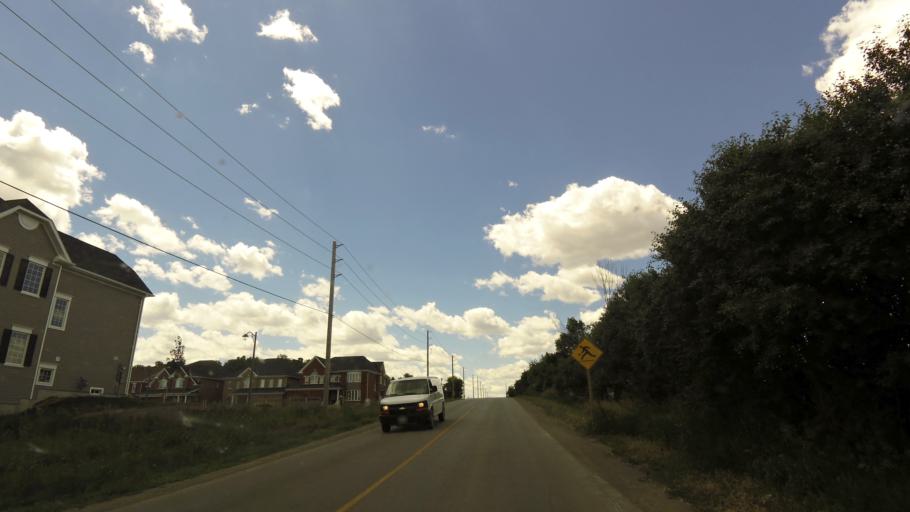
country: CA
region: Ontario
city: Oshawa
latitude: 43.9607
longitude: -78.8400
